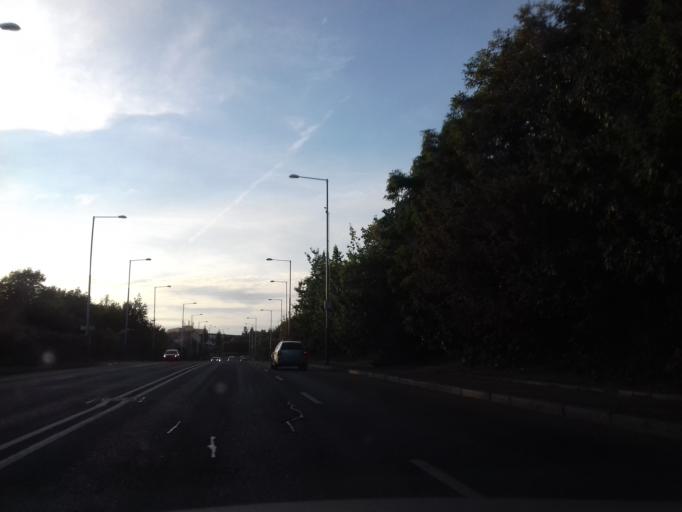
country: CZ
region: Praha
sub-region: Praha 4
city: Hodkovicky
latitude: 50.0381
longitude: 14.4430
